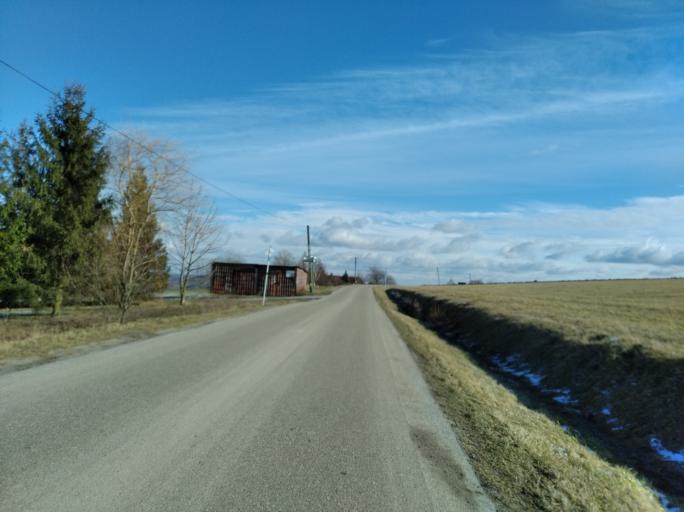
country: PL
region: Subcarpathian Voivodeship
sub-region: Powiat ropczycko-sedziszowski
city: Wielopole Skrzynskie
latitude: 49.9167
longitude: 21.6330
